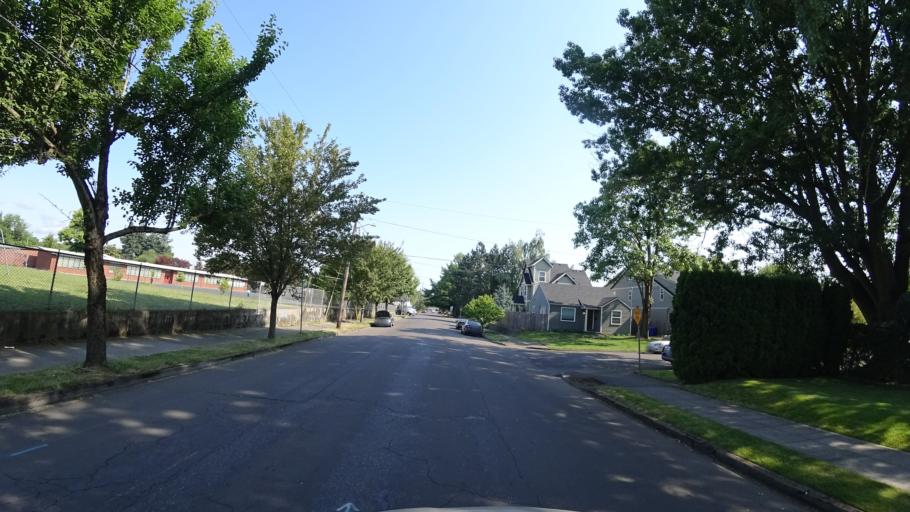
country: US
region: Oregon
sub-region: Washington County
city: West Haven
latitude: 45.5951
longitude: -122.7349
